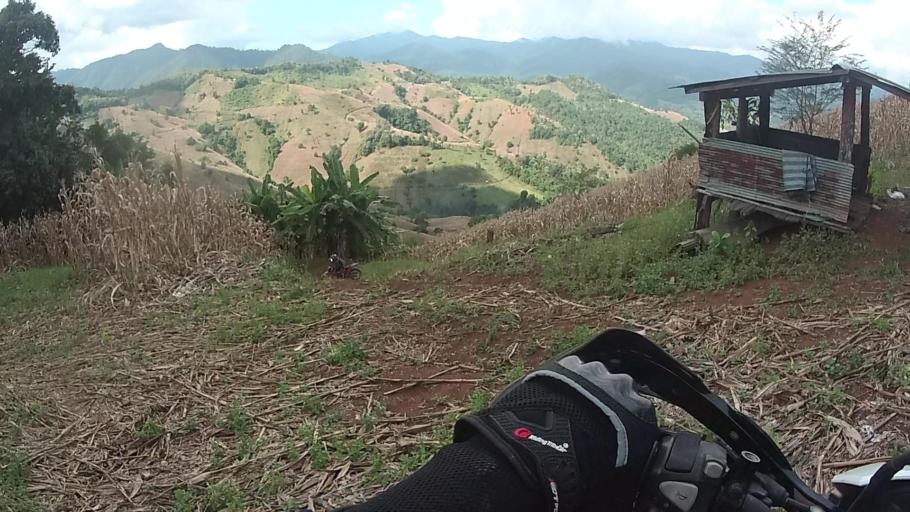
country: TH
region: Lampang
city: Wang Nuea
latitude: 19.0930
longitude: 99.4873
